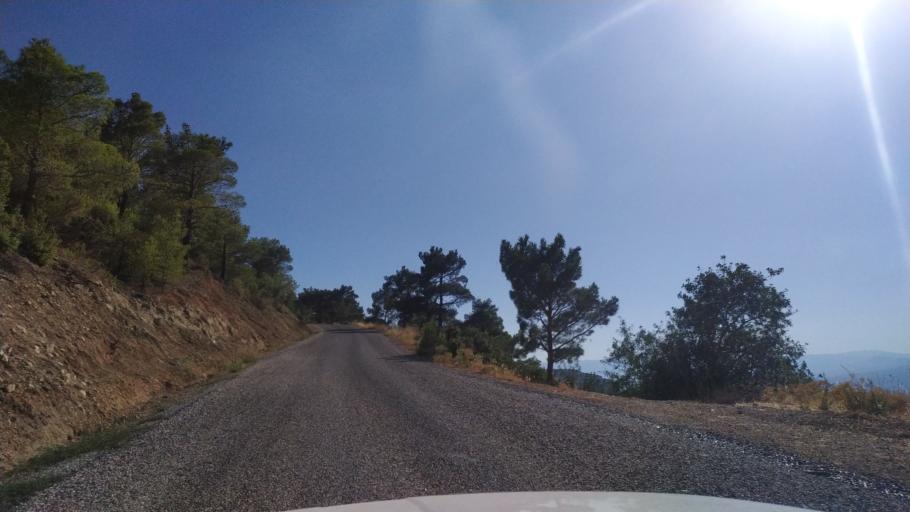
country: TR
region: Mersin
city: Mut
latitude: 36.7039
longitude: 33.4731
